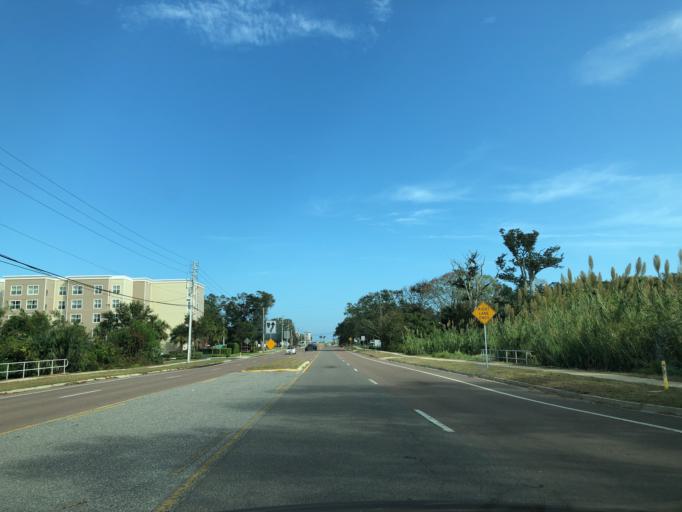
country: US
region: Florida
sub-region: Nassau County
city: Fernandina Beach
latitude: 30.6396
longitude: -81.4430
